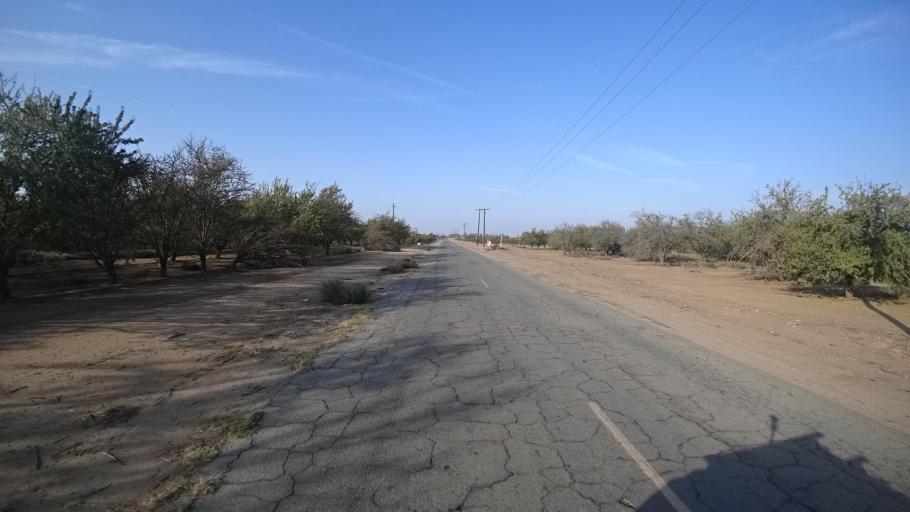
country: US
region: California
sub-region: Kern County
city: McFarland
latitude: 35.6818
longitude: -119.2126
